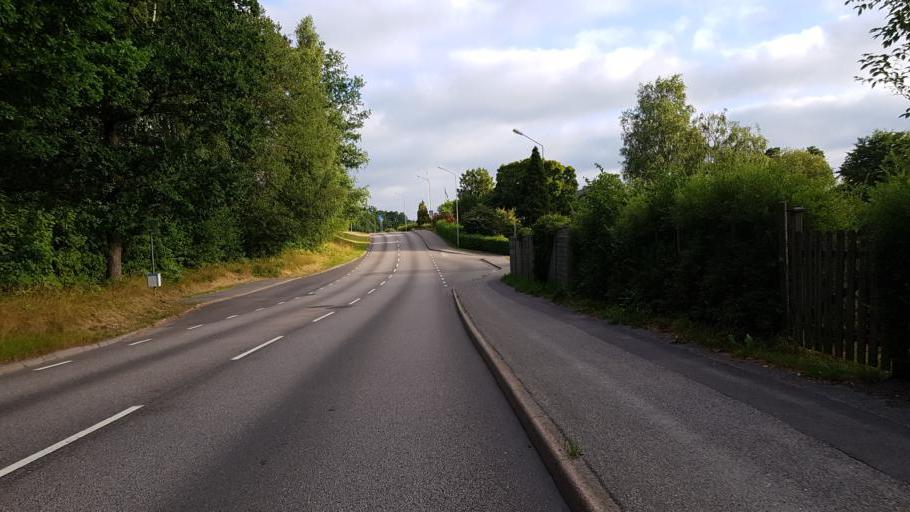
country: SE
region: Vaestra Goetaland
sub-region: Harryda Kommun
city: Molnlycke
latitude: 57.6508
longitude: 12.1108
